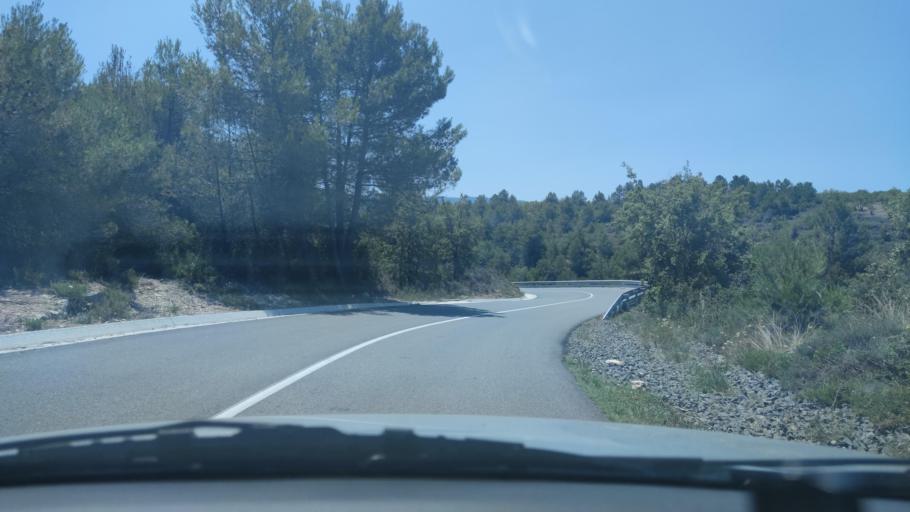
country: ES
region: Catalonia
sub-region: Provincia de Lleida
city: Vinaixa
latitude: 41.4144
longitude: 0.9562
